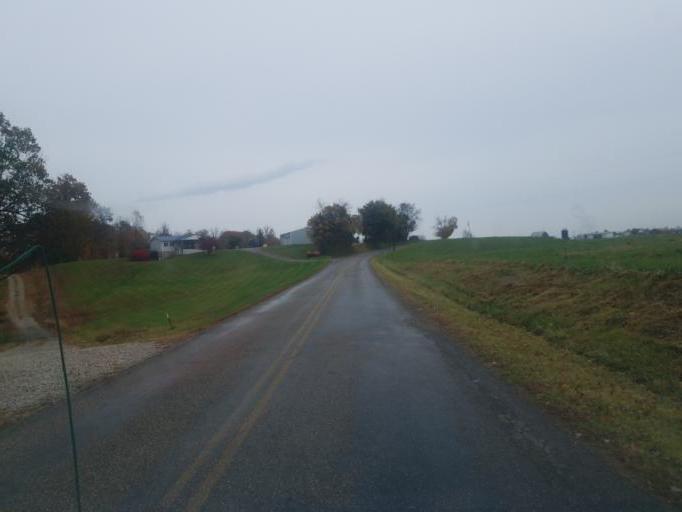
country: US
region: Ohio
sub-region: Washington County
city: Beverly
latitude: 39.5529
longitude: -81.7039
